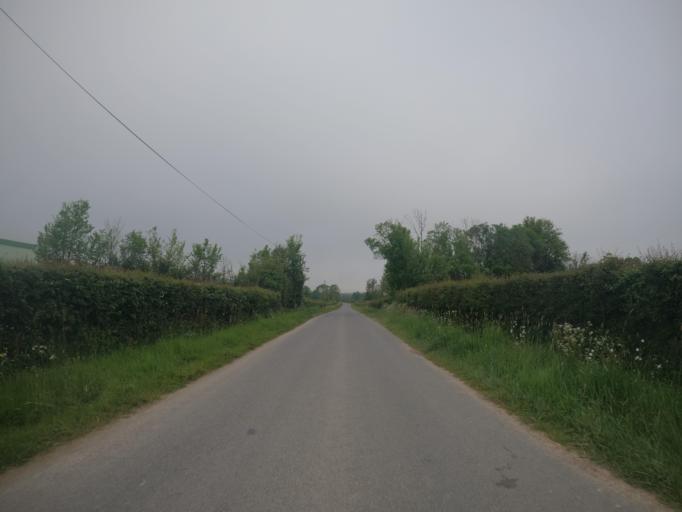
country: FR
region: Poitou-Charentes
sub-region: Departement des Deux-Sevres
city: Chiche
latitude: 46.8538
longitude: -0.3406
